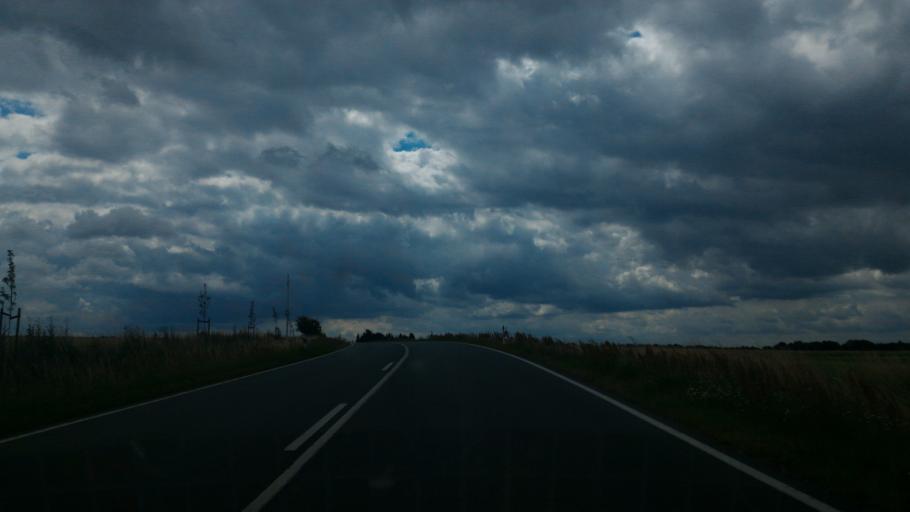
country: DE
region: Saxony
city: Goerlitz
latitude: 51.1993
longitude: 14.9447
